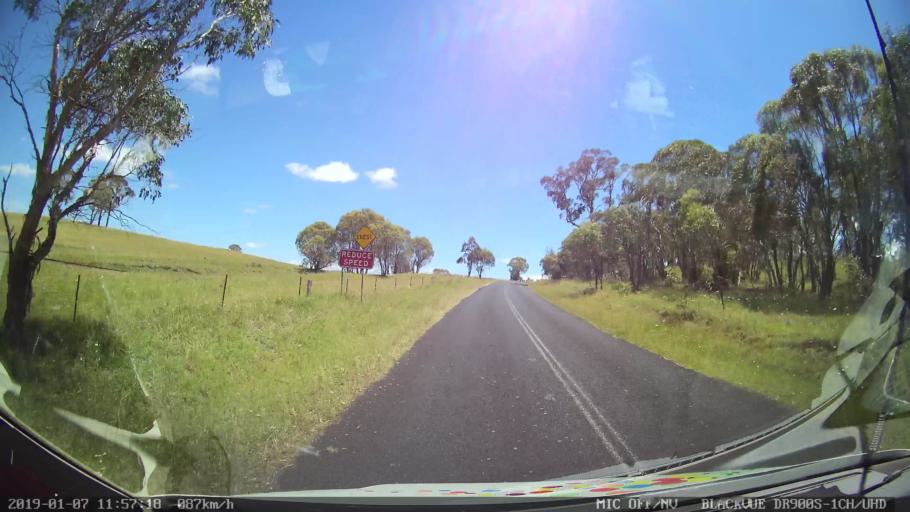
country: AU
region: New South Wales
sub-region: Guyra
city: Guyra
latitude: -30.2660
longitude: 151.6663
